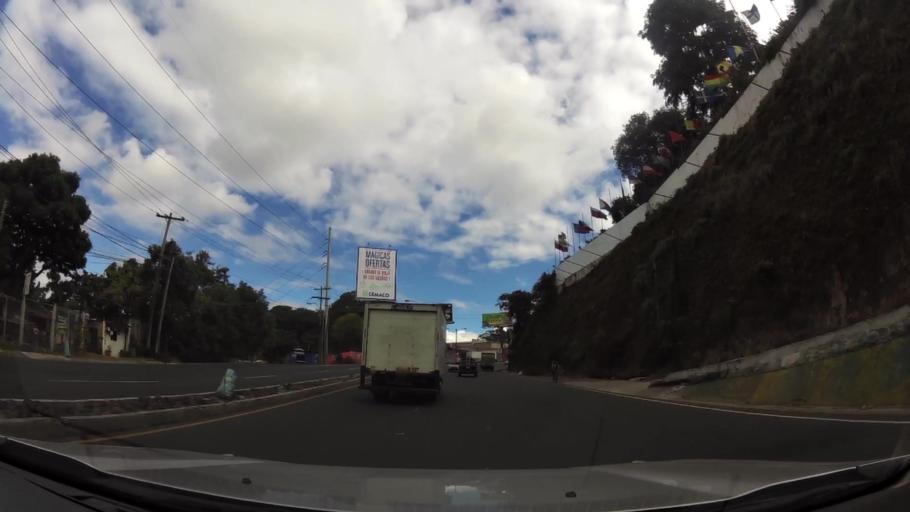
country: GT
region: Guatemala
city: Mixco
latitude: 14.6250
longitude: -90.6065
